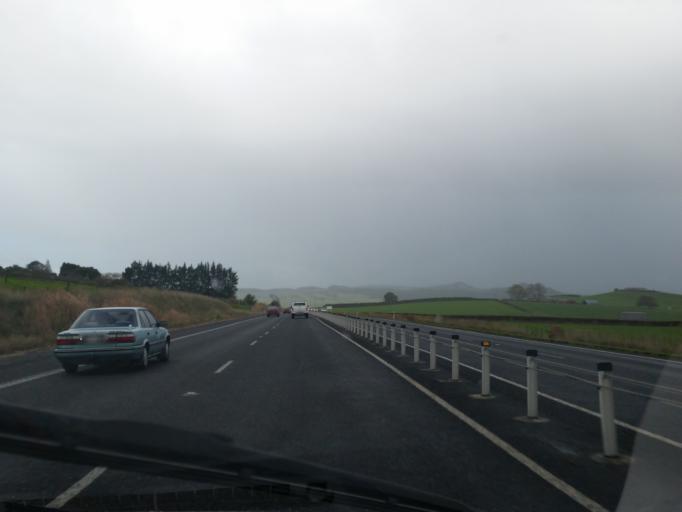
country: NZ
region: Waikato
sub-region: Waikato District
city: Te Kauwhata
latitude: -37.2808
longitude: 175.2988
